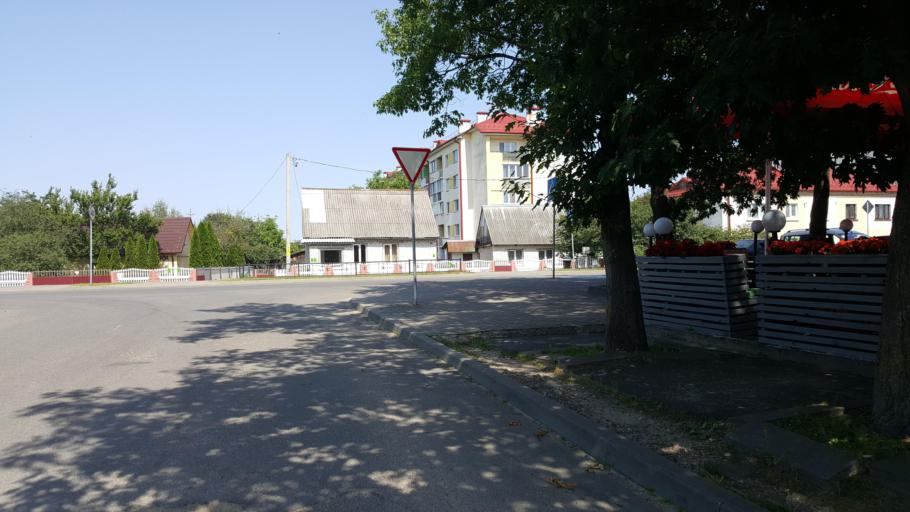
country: BY
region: Brest
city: Zhabinka
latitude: 52.1943
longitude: 24.0172
